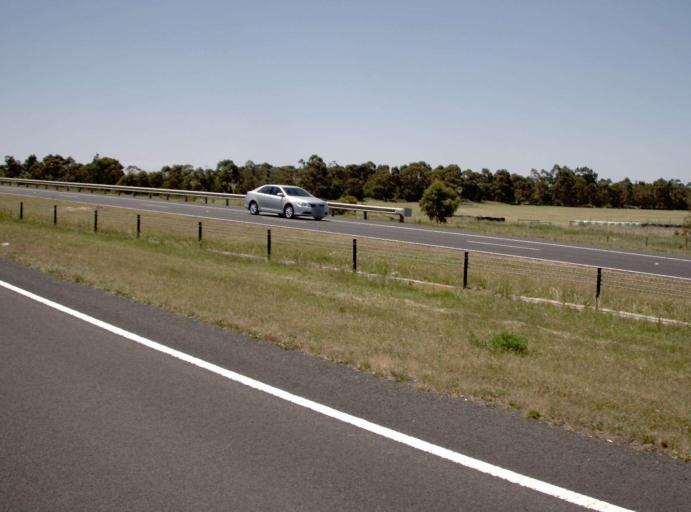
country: AU
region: Victoria
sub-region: Cardinia
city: Pakenham South
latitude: -38.0899
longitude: 145.5014
